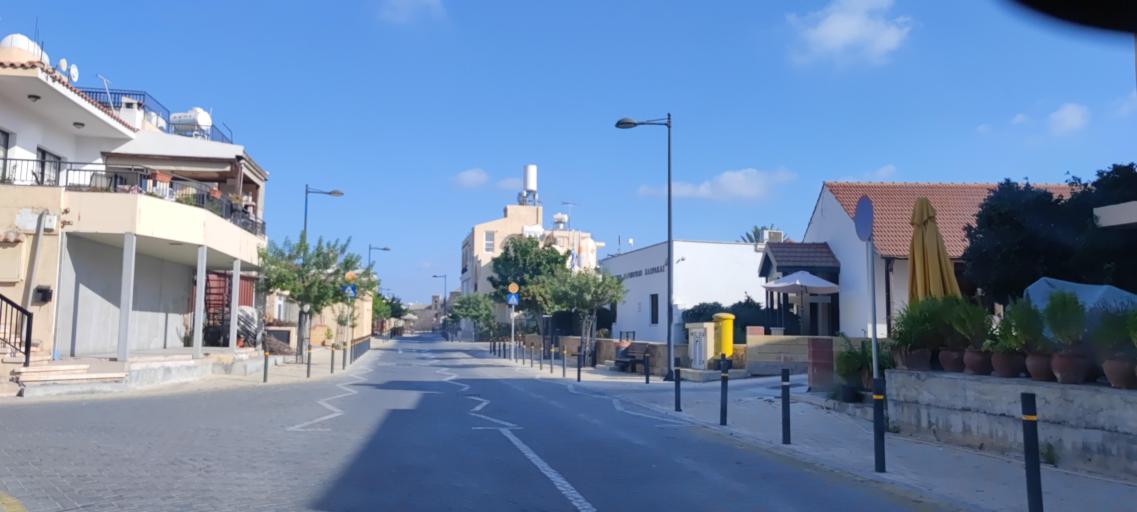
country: CY
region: Pafos
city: Chlorakas
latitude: 34.7980
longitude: 32.4088
